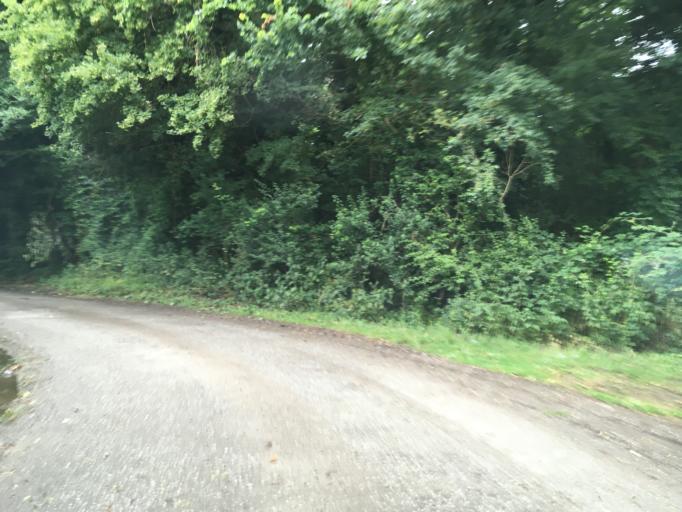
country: GB
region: England
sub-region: Gloucestershire
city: Cinderford
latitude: 51.7970
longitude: -2.4114
